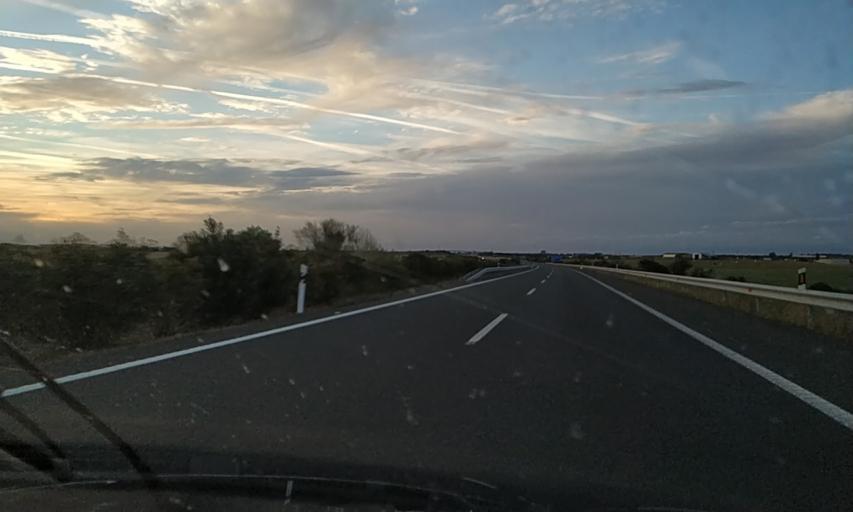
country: ES
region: Extremadura
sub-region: Provincia de Caceres
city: Aldea del Cano
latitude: 39.2739
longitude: -6.3227
